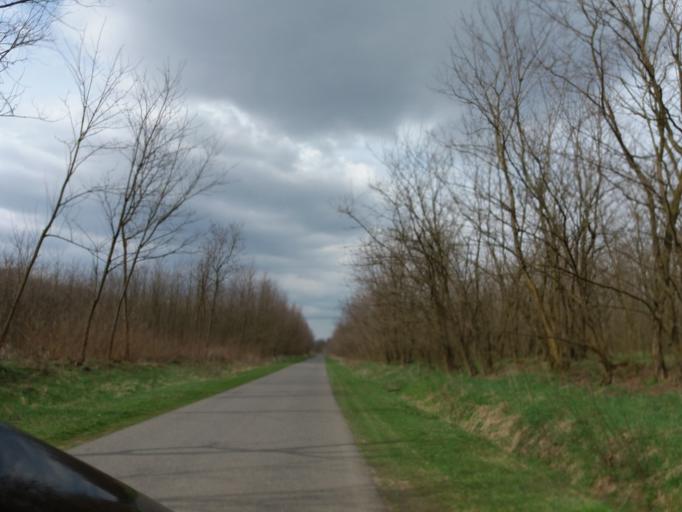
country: HU
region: Szabolcs-Szatmar-Bereg
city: Petnehaza
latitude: 48.0731
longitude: 22.0442
